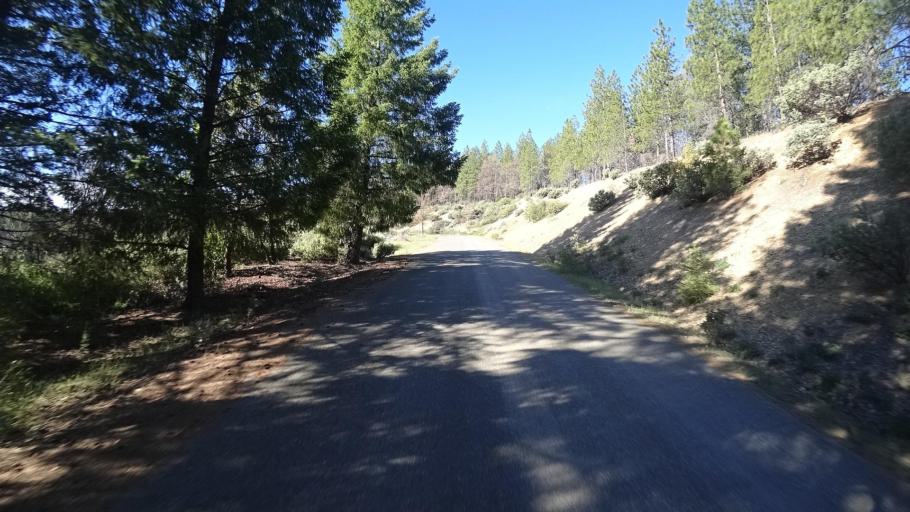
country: US
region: California
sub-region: Lake County
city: Upper Lake
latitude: 39.3165
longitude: -122.9469
